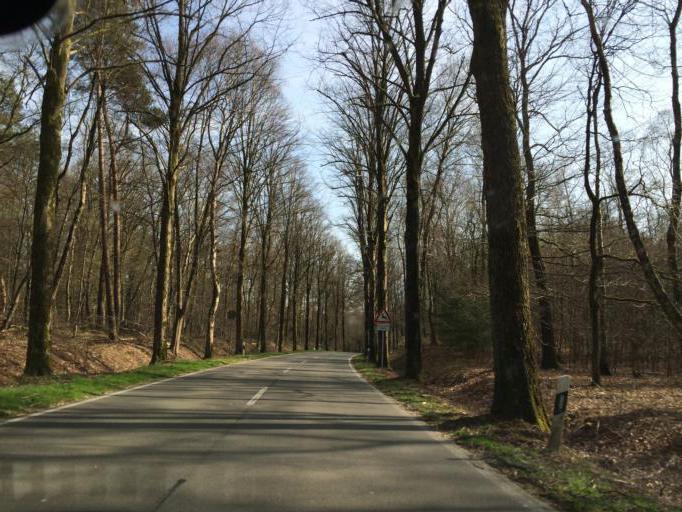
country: DE
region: North Rhine-Westphalia
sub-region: Regierungsbezirk Munster
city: Klein Reken
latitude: 51.7729
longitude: 7.1082
